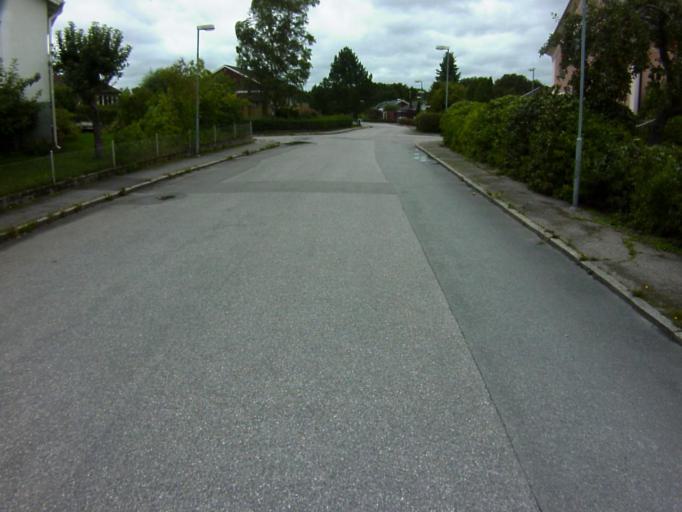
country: SE
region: Soedermanland
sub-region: Eskilstuna Kommun
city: Eskilstuna
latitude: 59.3796
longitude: 16.4733
